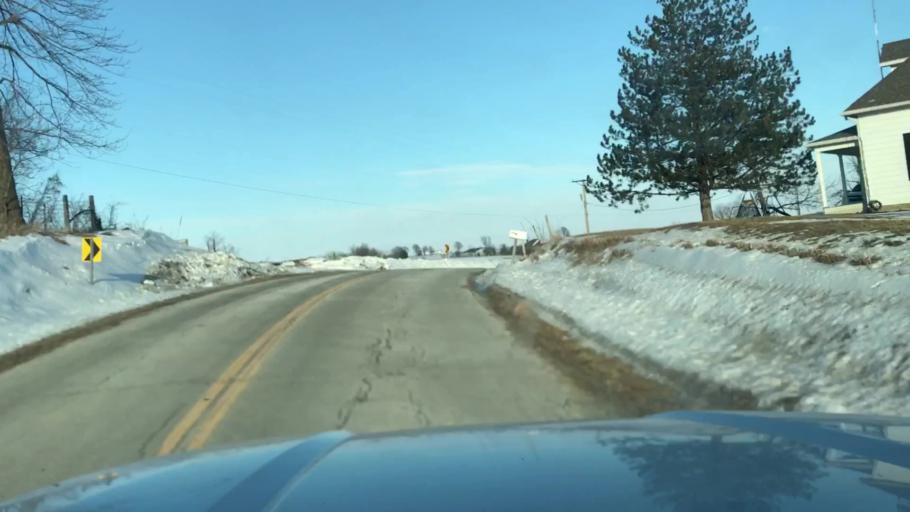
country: US
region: Missouri
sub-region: Andrew County
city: Savannah
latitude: 40.0243
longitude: -94.9141
